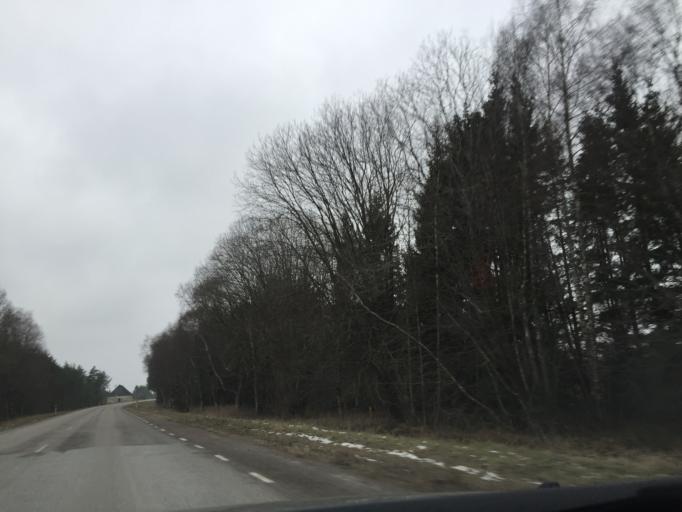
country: EE
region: Saare
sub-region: Kuressaare linn
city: Kuressaare
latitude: 58.2889
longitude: 22.3200
